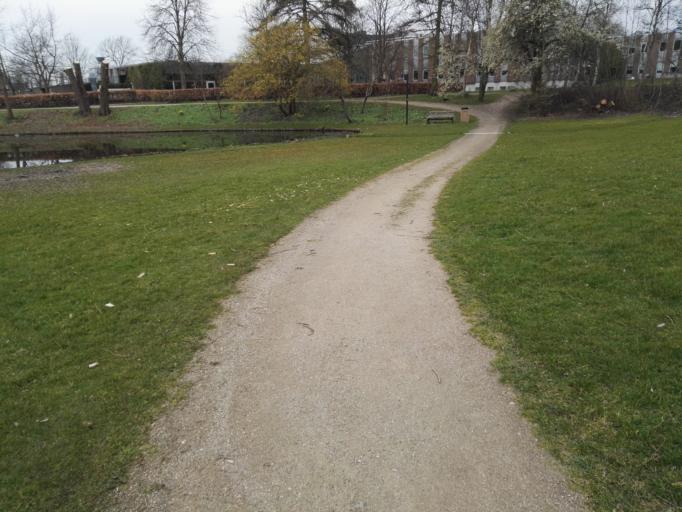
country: DK
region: Capital Region
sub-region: Ballerup Kommune
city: Ballerup
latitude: 55.7327
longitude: 12.3661
